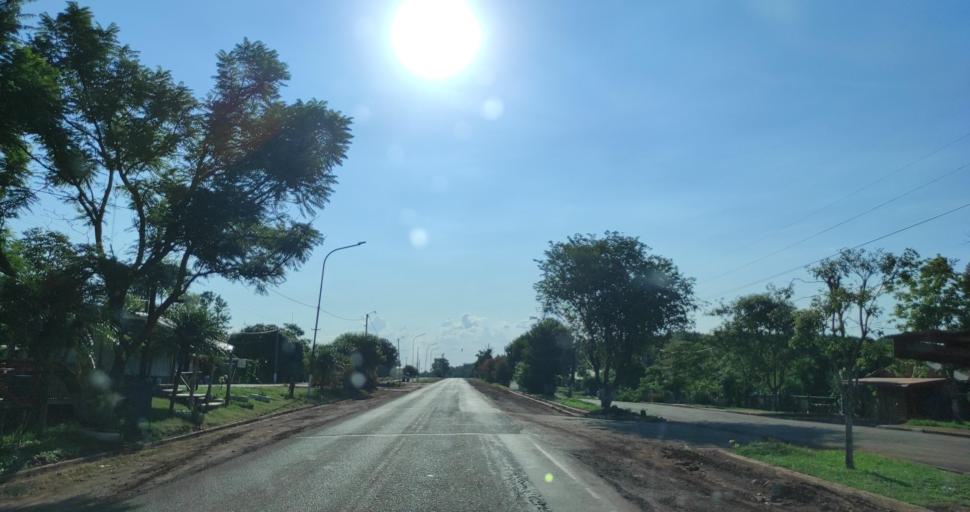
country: AR
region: Misiones
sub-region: Departamento de Eldorado
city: Eldorado
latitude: -26.4002
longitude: -54.4132
